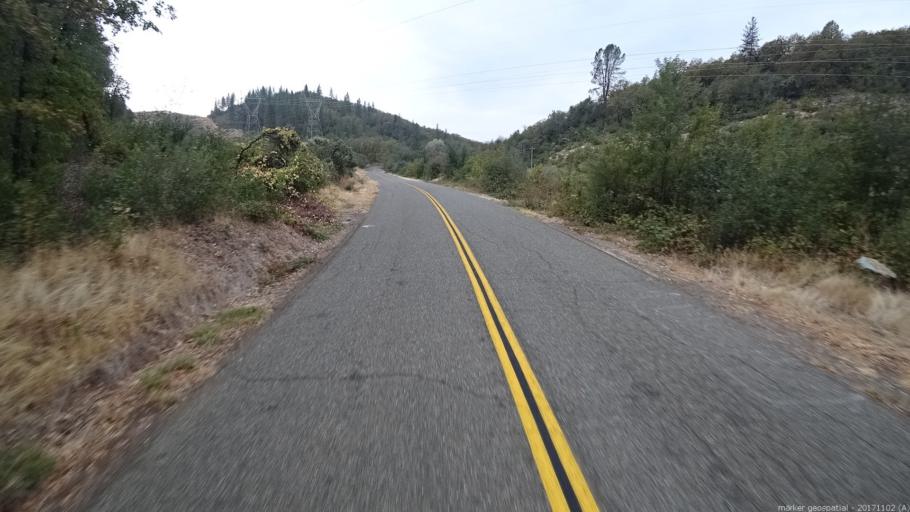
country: US
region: California
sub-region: Shasta County
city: Central Valley (historical)
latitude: 40.6579
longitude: -122.4211
